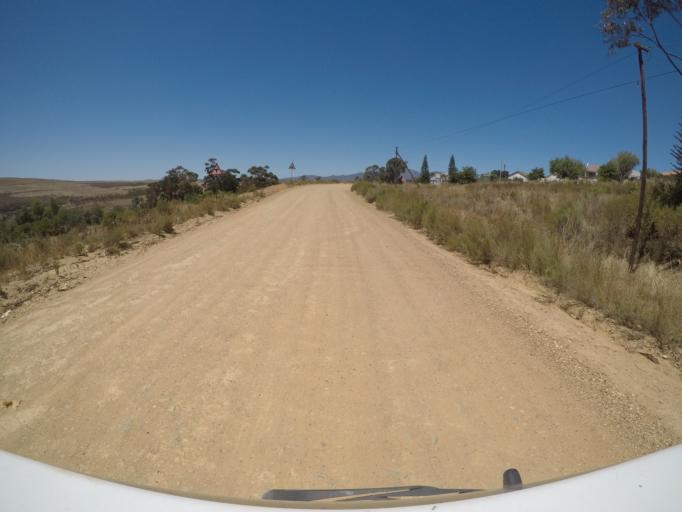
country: ZA
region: Western Cape
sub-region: Overberg District Municipality
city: Hermanus
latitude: -34.2233
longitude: 19.2046
